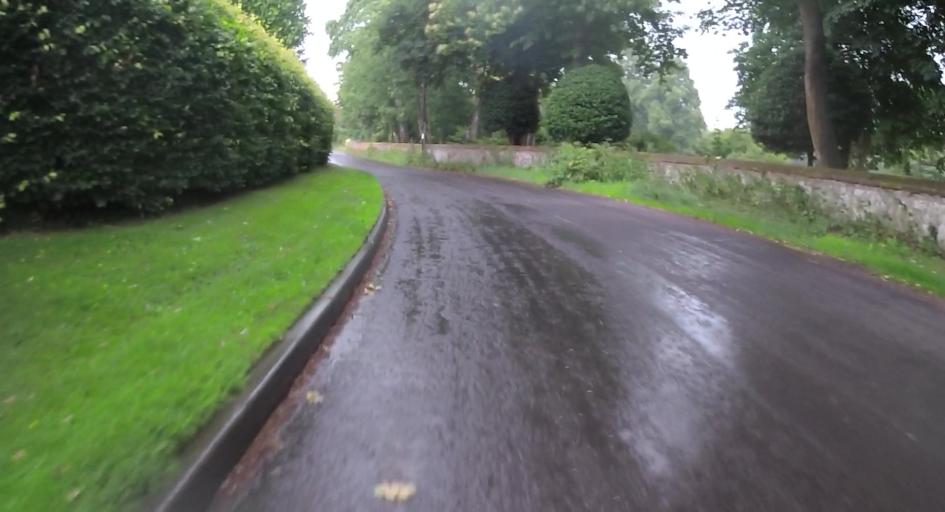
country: GB
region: England
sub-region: Hampshire
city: Long Sutton
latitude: 51.1808
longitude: -0.9197
